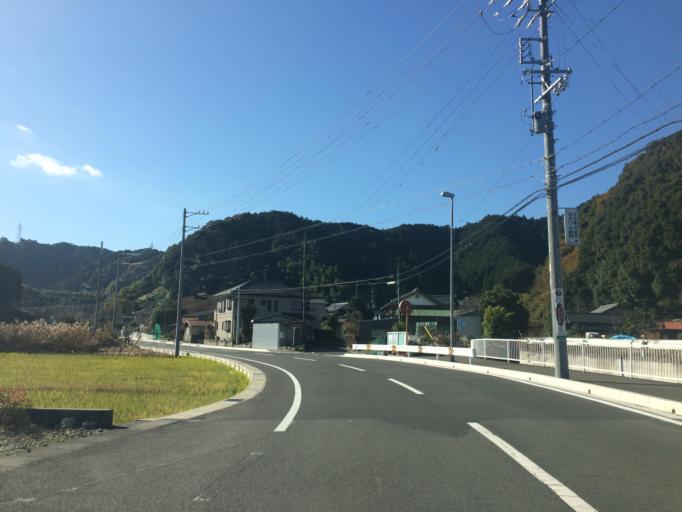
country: JP
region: Shizuoka
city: Shizuoka-shi
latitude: 34.9872
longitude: 138.2949
